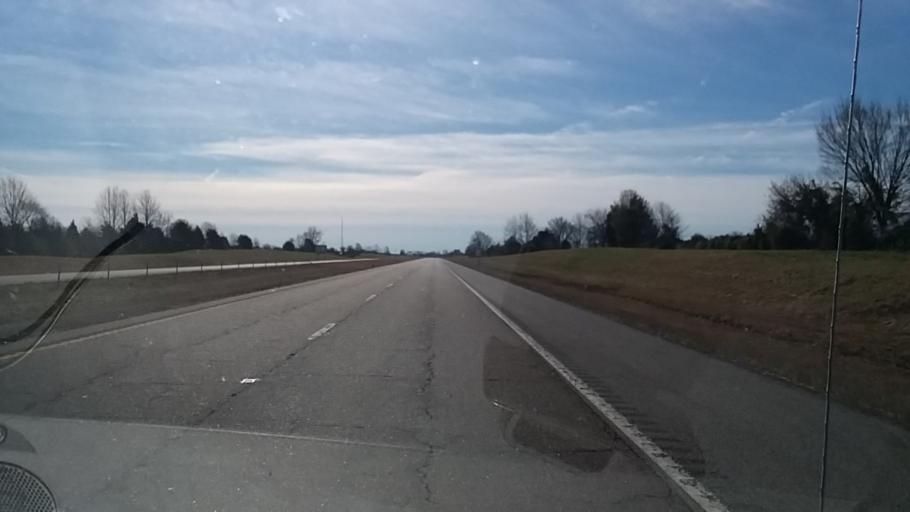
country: US
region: Tennessee
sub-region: Crockett County
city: Alamo
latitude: 35.7893
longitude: -89.1539
